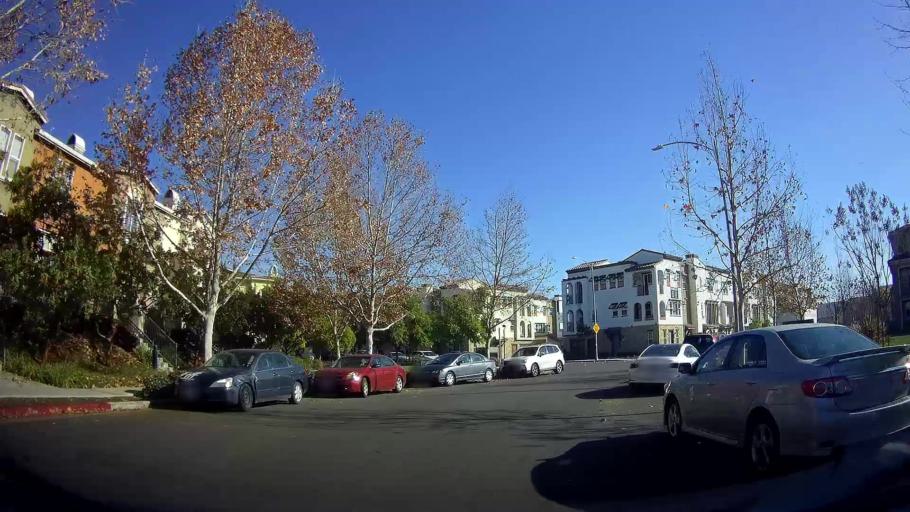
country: US
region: California
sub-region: Santa Clara County
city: Seven Trees
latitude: 37.2912
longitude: -121.8552
